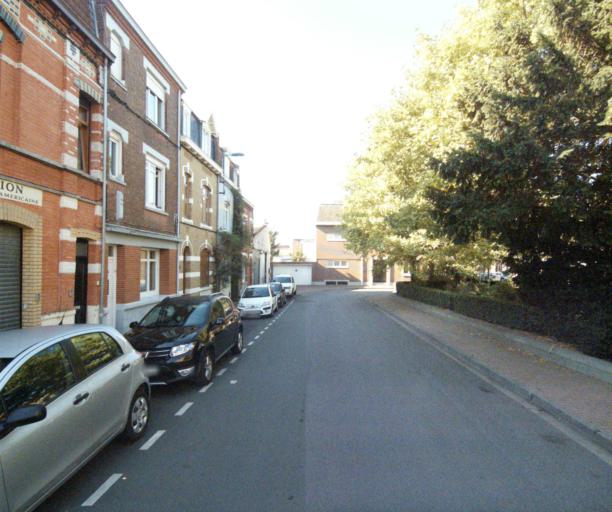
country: FR
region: Nord-Pas-de-Calais
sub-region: Departement du Nord
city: Mons-en-Baroeul
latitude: 50.6268
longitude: 3.1153
